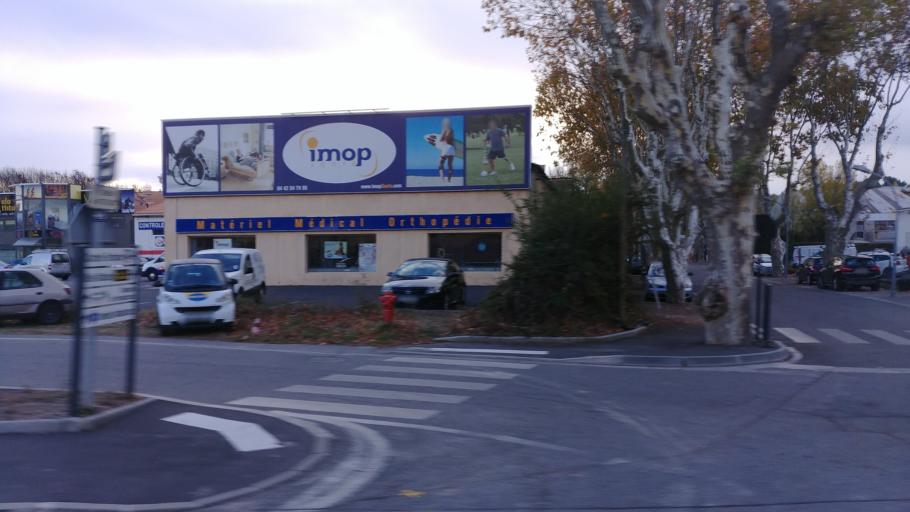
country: FR
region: Provence-Alpes-Cote d'Azur
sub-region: Departement des Bouches-du-Rhone
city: Venelles
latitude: 43.5859
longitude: 5.4749
